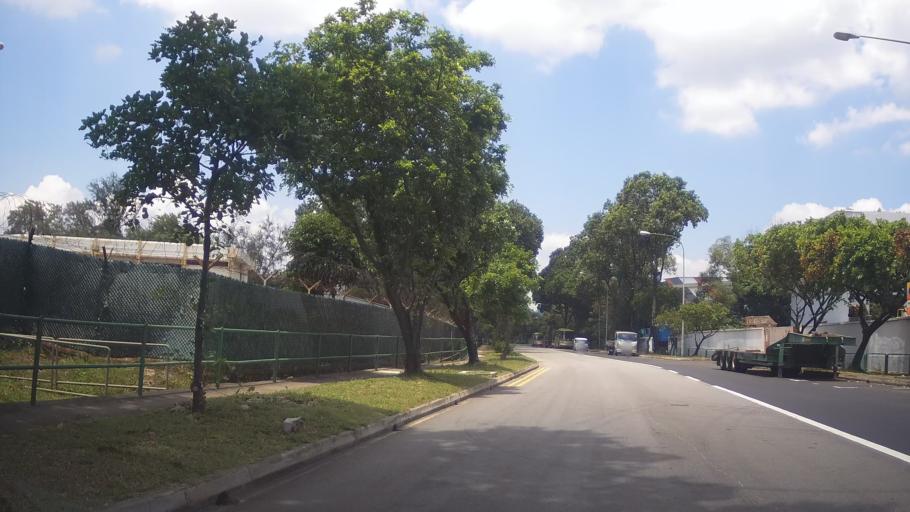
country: SG
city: Singapore
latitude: 1.2990
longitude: 103.6643
